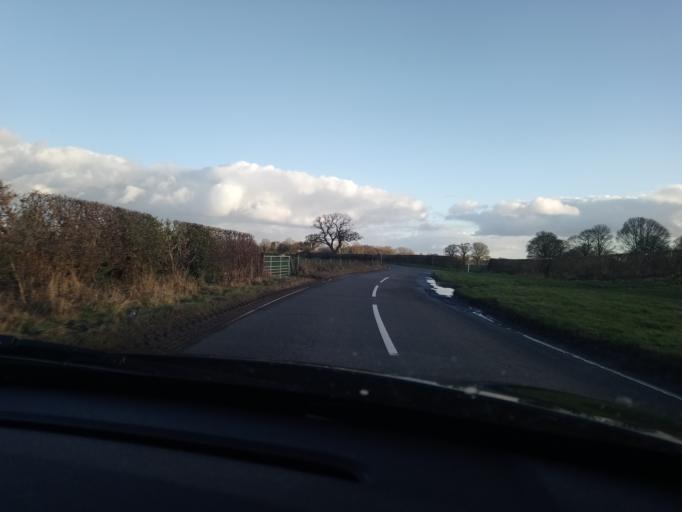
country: GB
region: England
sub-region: Shropshire
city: Ellesmere
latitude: 52.9030
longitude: -2.8146
